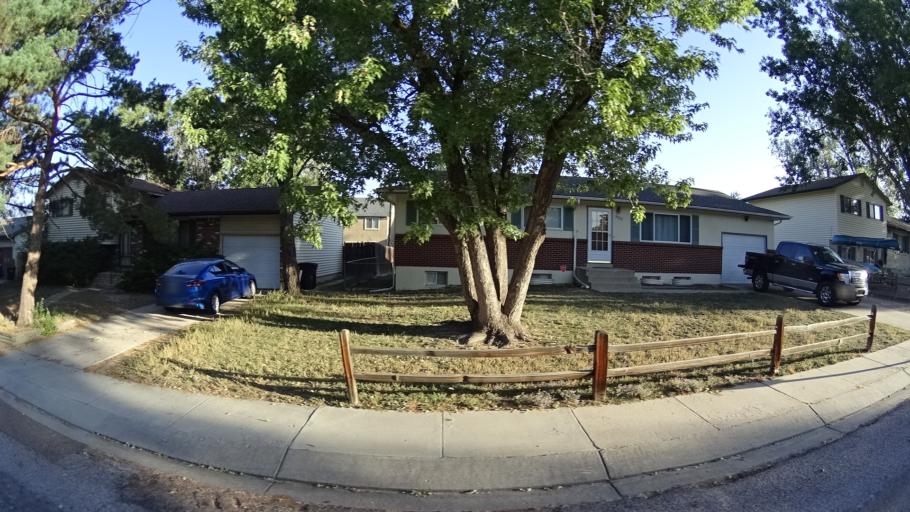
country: US
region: Colorado
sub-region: El Paso County
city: Cimarron Hills
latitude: 38.8893
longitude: -104.7525
